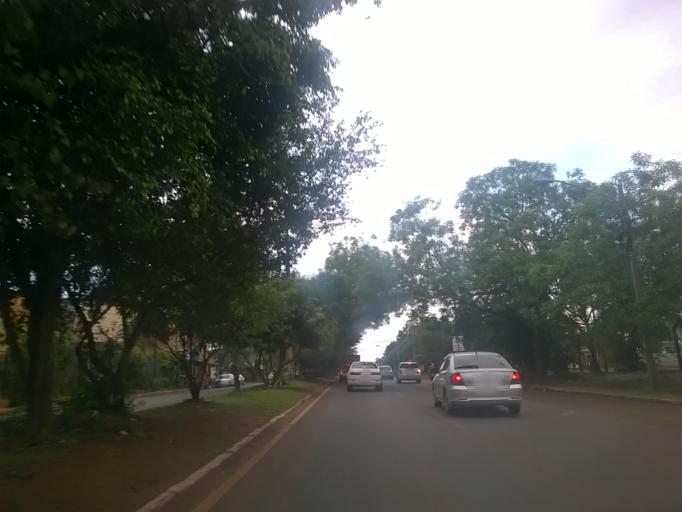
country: PY
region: Alto Parana
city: Presidente Franco
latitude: -25.5339
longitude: -54.6337
